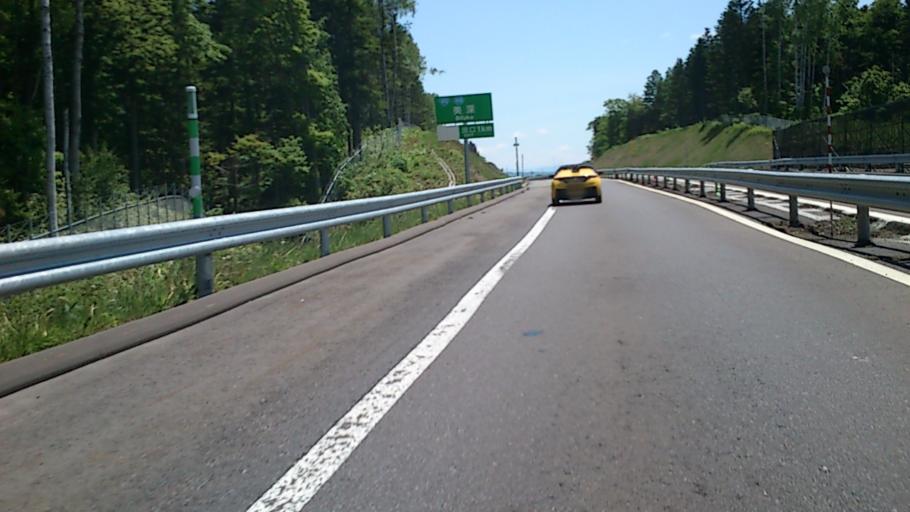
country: JP
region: Hokkaido
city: Nayoro
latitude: 44.4853
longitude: 142.3632
